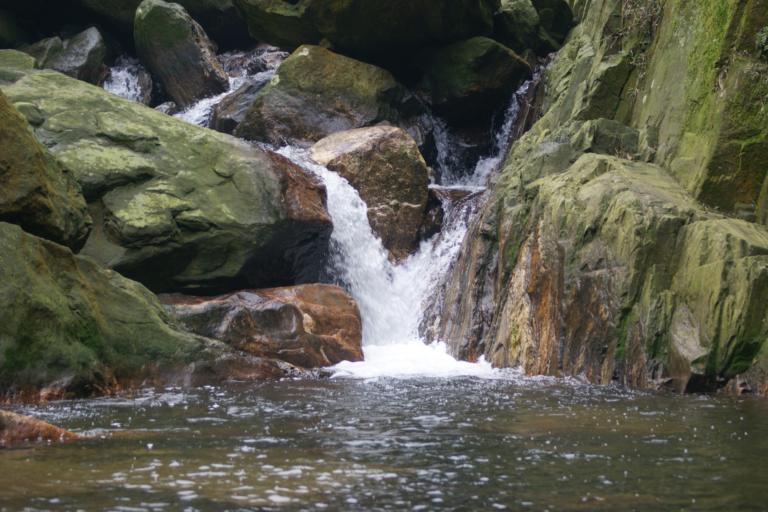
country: BR
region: Sao Paulo
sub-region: Rio Grande Da Serra
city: Rio Grande da Serra
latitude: -23.7933
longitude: -46.3716
